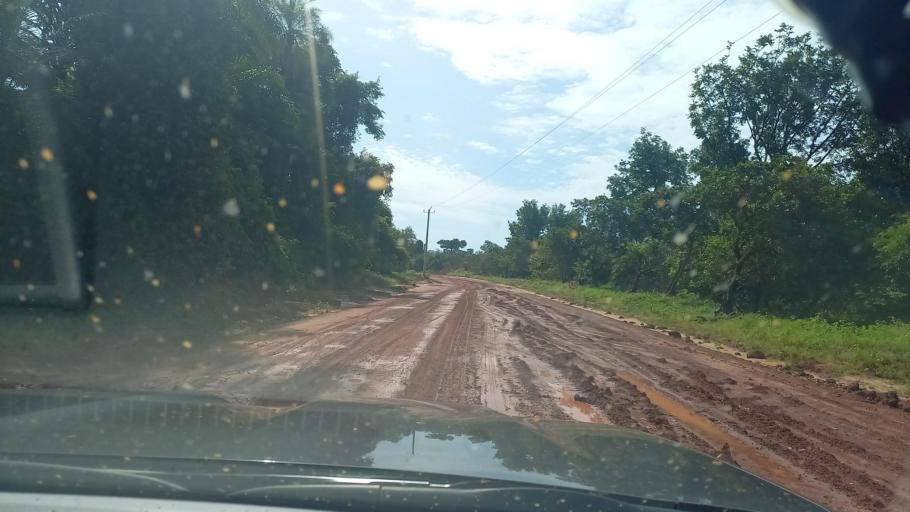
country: SN
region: Ziguinchor
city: Ziguinchor
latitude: 12.6718
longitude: -16.1902
